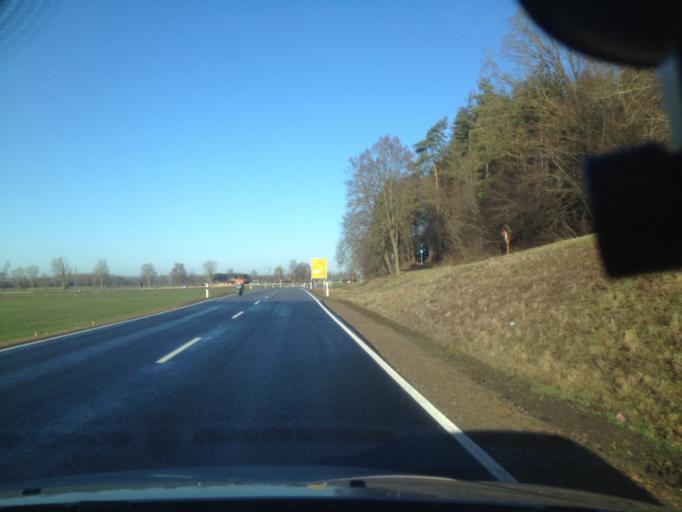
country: DE
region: Bavaria
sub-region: Swabia
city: Haldenwang
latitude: 48.4414
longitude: 10.4296
